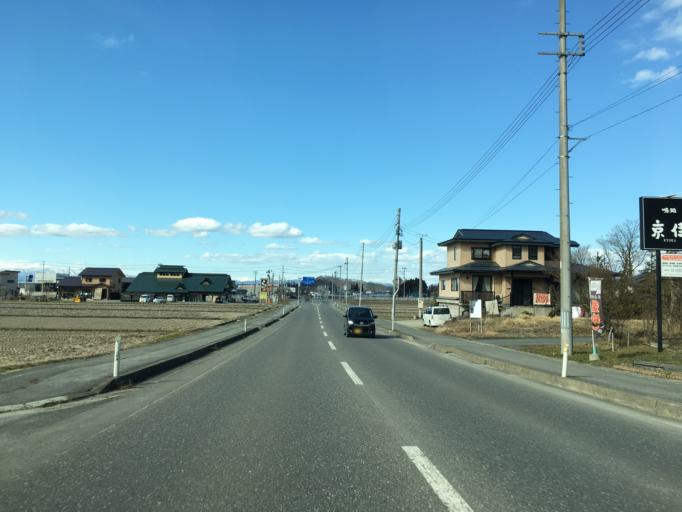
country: JP
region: Yamagata
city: Yonezawa
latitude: 37.9076
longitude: 140.1464
